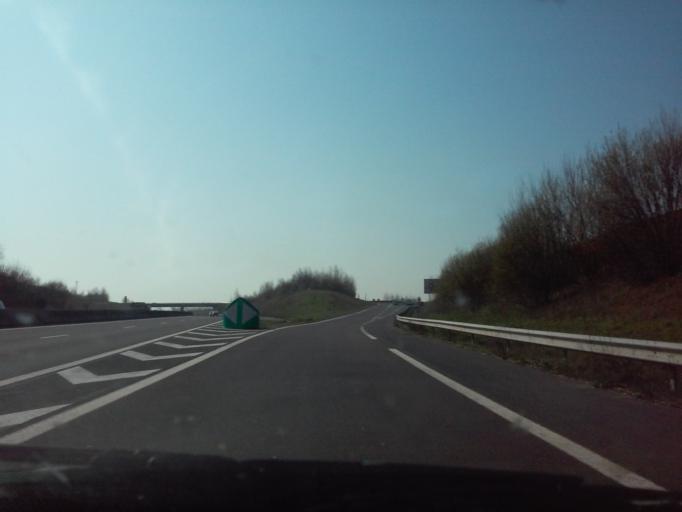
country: FR
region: Lower Normandy
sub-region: Departement du Calvados
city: Saint-Vigor-le-Grand
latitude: 49.2526
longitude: -0.6447
